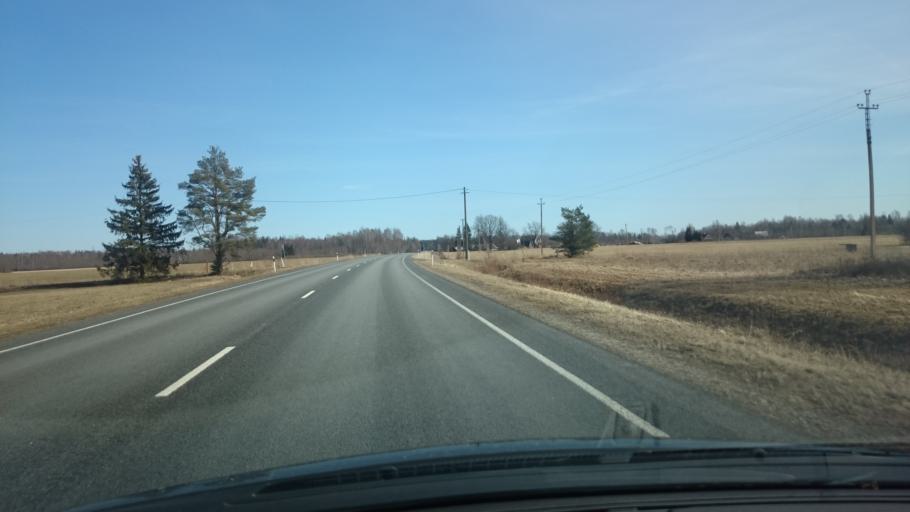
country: EE
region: Paernumaa
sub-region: Vaendra vald (alev)
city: Vandra
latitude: 58.6681
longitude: 25.0514
